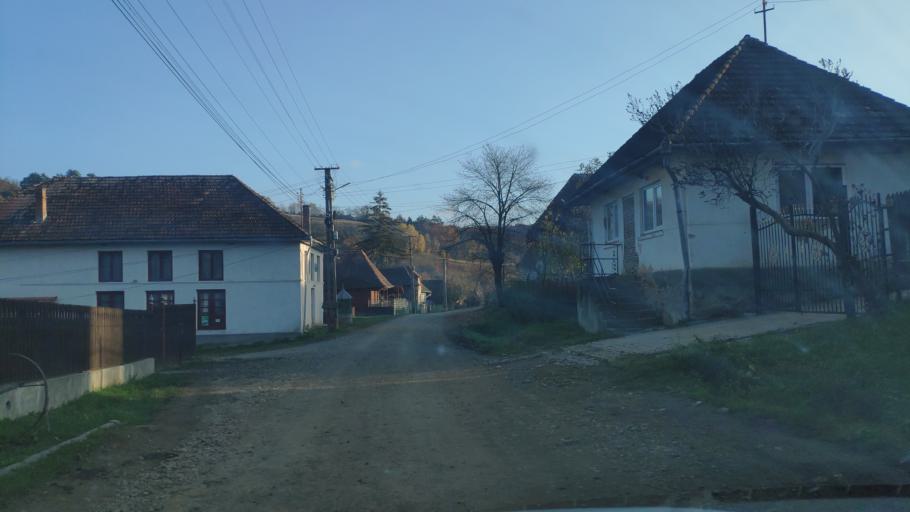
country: RO
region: Mures
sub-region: Comuna Ghindari
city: Ghindari
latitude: 46.5253
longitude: 24.9144
